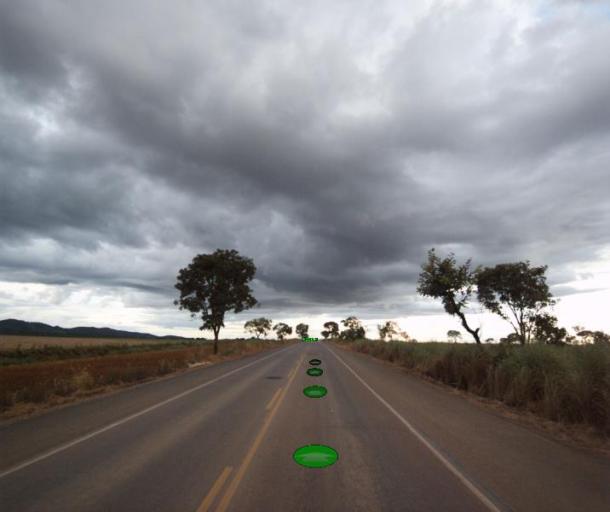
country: BR
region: Goias
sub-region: Uruacu
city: Uruacu
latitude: -14.7093
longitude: -49.2244
